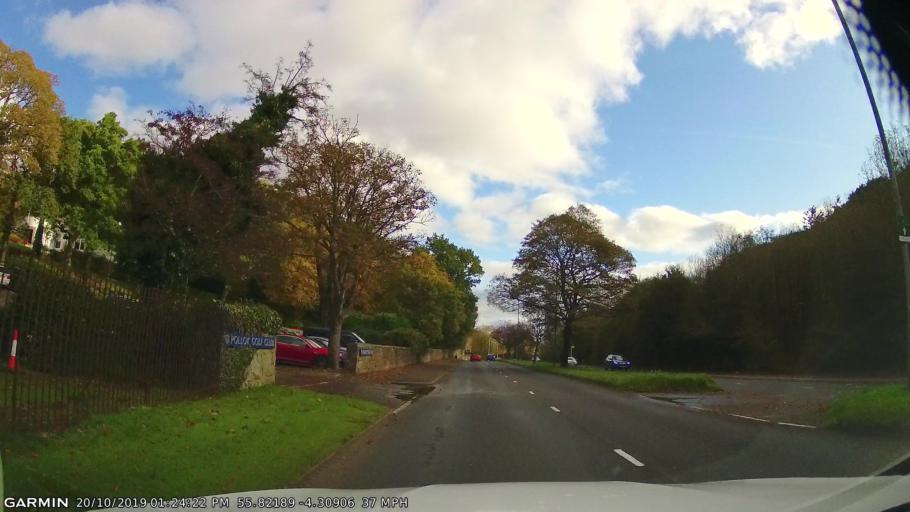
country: GB
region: Scotland
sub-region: East Renfrewshire
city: Giffnock
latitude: 55.8219
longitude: -4.3091
